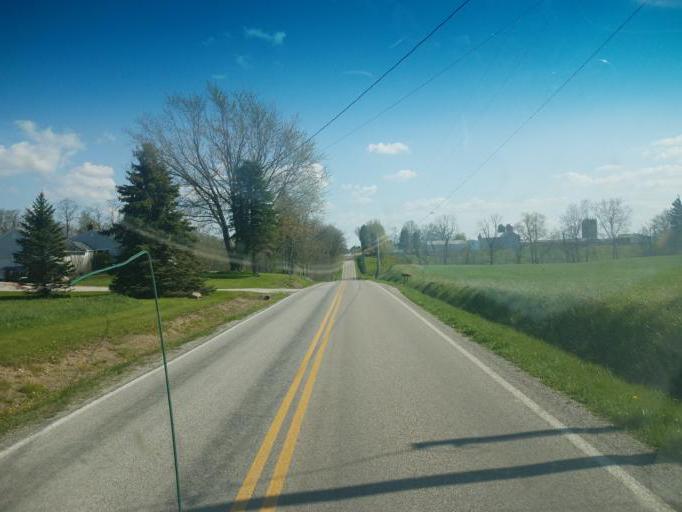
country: US
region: Ohio
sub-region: Wayne County
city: Creston
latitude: 40.9533
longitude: -81.9571
